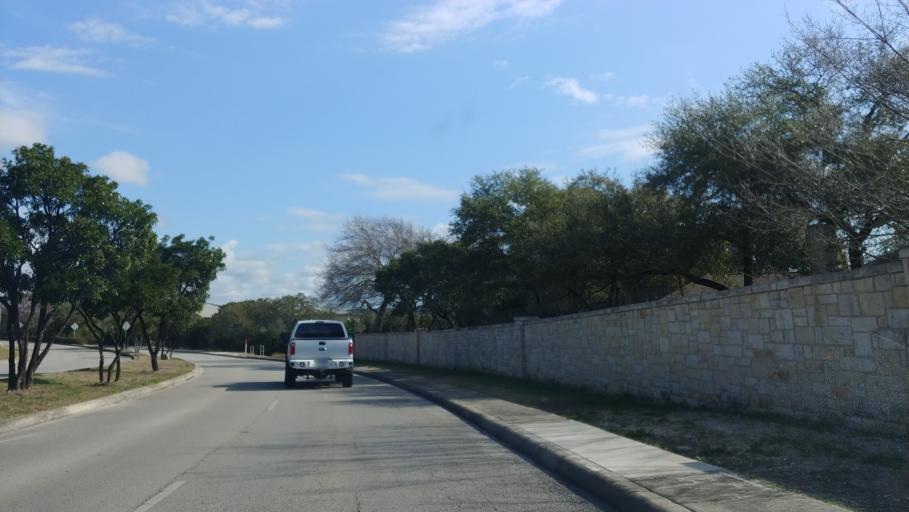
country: US
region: Texas
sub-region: Bexar County
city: Cross Mountain
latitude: 29.6175
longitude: -98.6128
